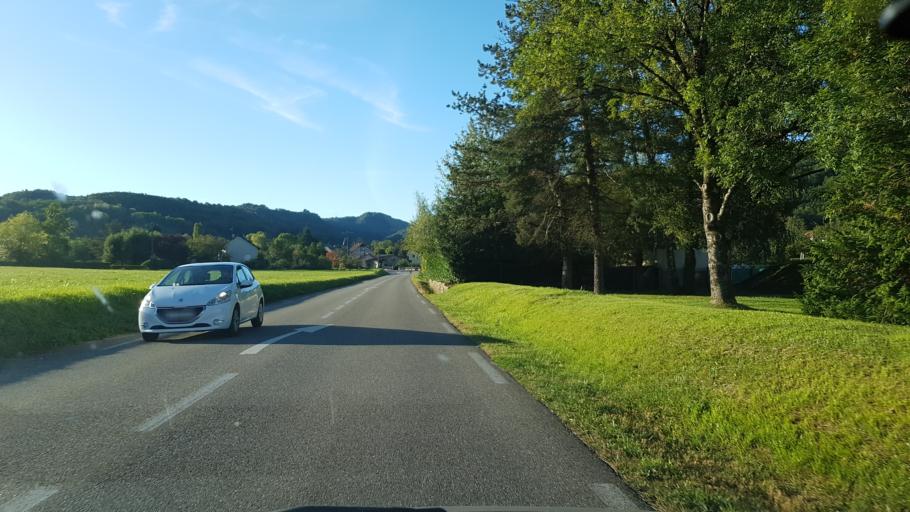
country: FR
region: Franche-Comte
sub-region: Departement du Jura
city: Lons-le-Saunier
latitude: 46.6515
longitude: 5.5382
